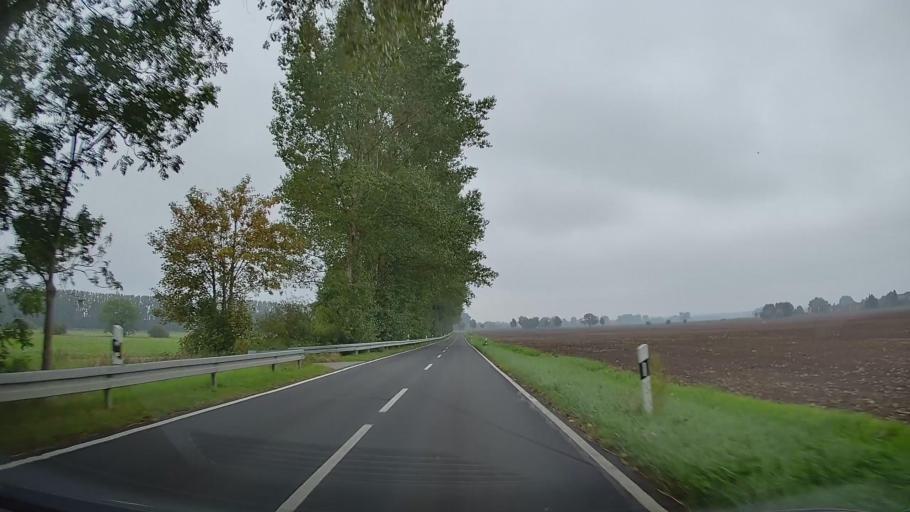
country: DE
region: Mecklenburg-Vorpommern
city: Biendorf
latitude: 54.0901
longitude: 11.6327
